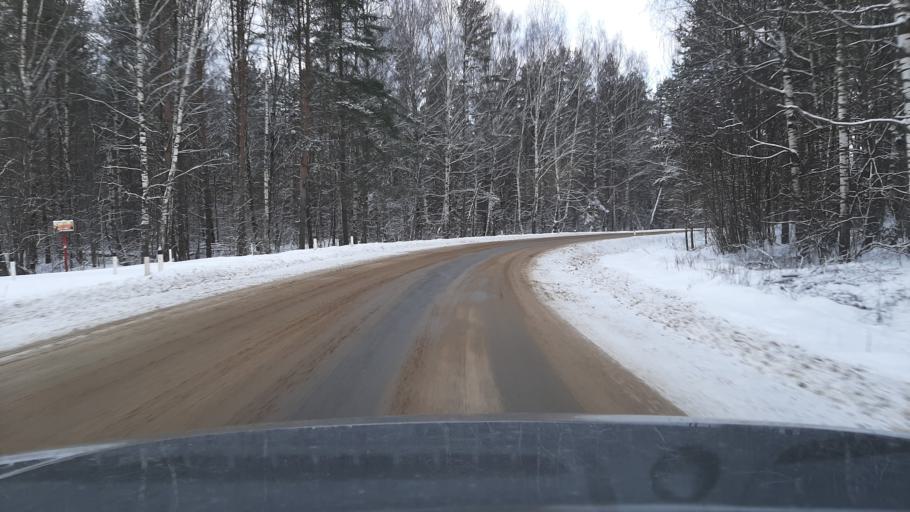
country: RU
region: Kostroma
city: Nerekhta
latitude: 57.4687
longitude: 40.6182
